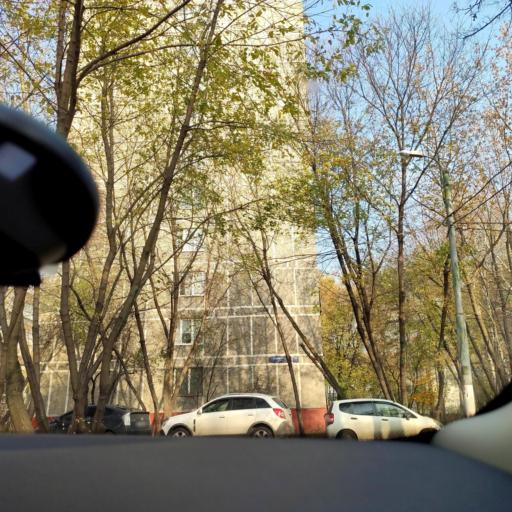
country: RU
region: Moscow
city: Kuz'minki
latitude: 55.6744
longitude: 37.8076
